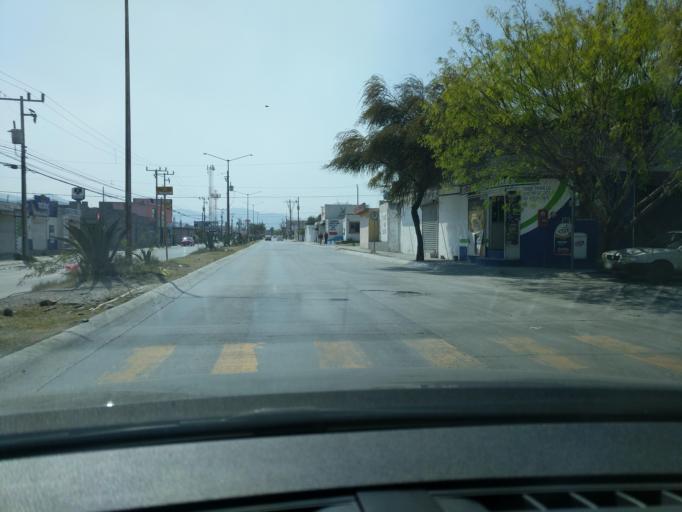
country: MX
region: Nuevo Leon
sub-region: Garcia
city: Valle de Lincoln
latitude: 25.7915
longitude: -100.4843
